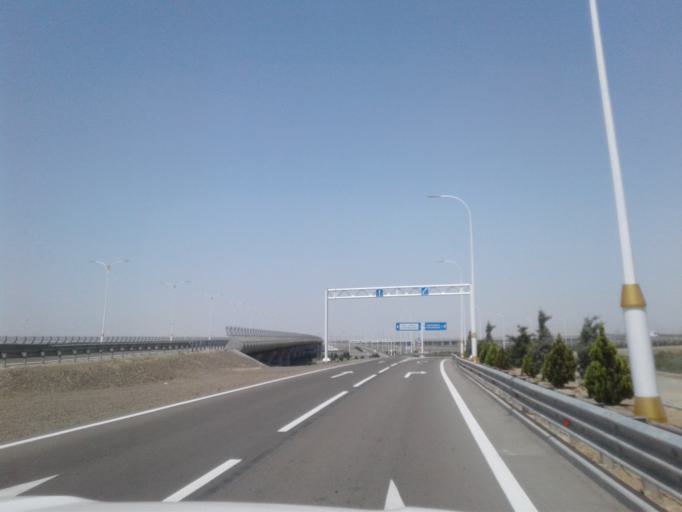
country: TM
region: Balkan
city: Turkmenbasy
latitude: 39.9785
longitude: 52.8693
